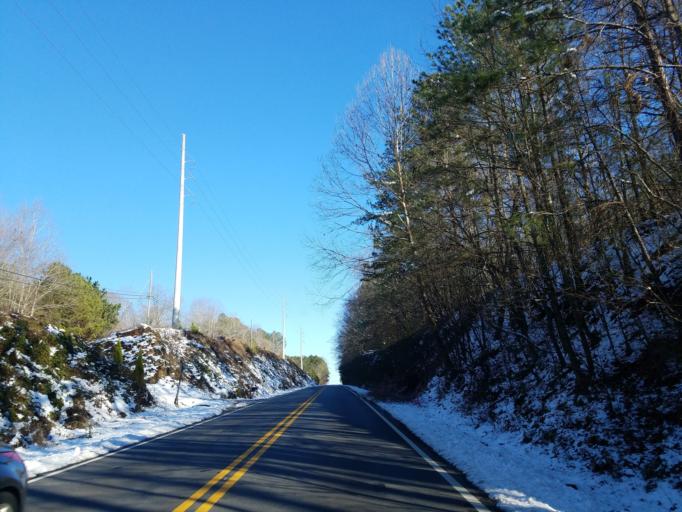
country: US
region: Georgia
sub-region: Dawson County
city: Dawsonville
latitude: 34.3540
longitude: -84.0912
